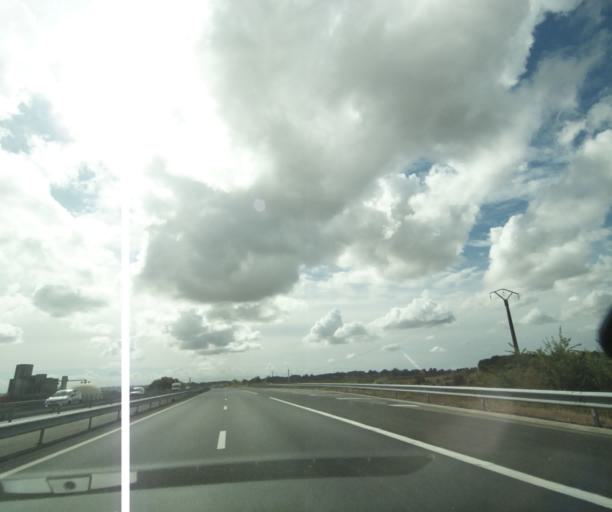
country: FR
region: Poitou-Charentes
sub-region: Departement de la Charente-Maritime
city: Chermignac
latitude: 45.7182
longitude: -0.6592
